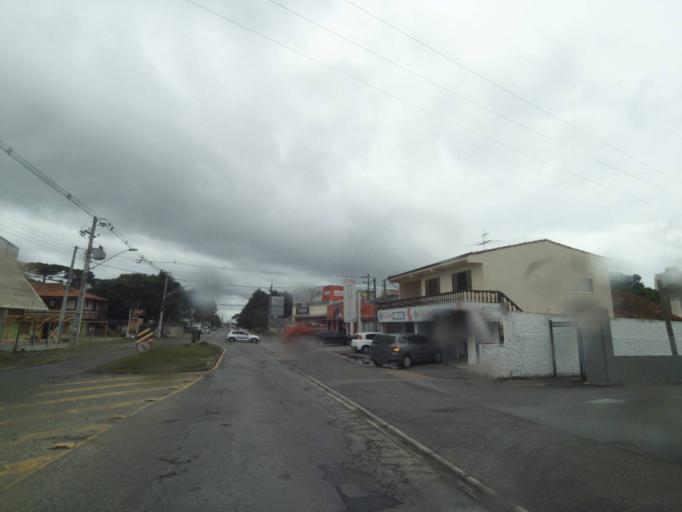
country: BR
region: Parana
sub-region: Curitiba
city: Curitiba
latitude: -25.4472
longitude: -49.3491
